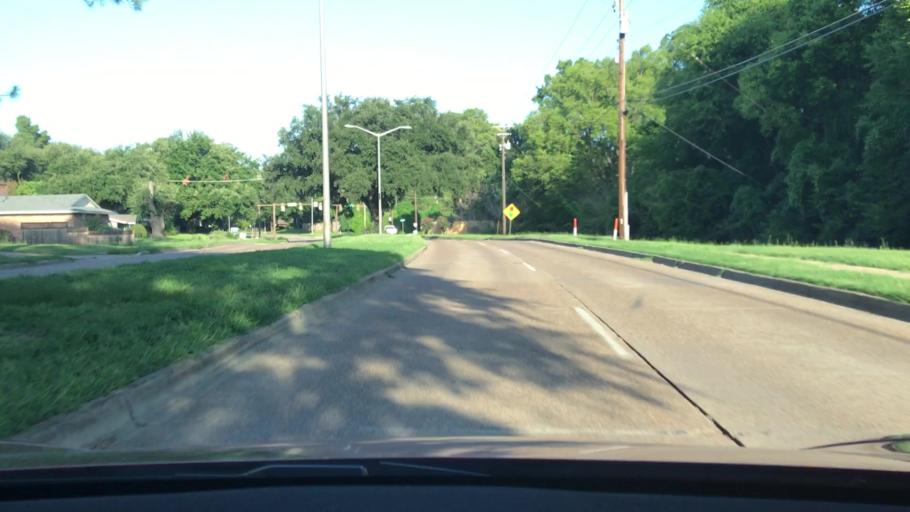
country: US
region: Louisiana
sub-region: Bossier Parish
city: Bossier City
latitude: 32.4567
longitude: -93.7271
